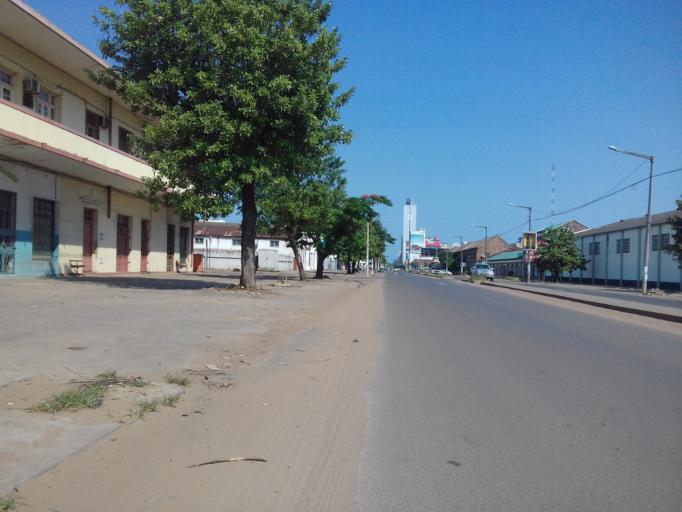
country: MZ
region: Maputo City
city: Maputo
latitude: -25.9666
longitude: 32.5606
